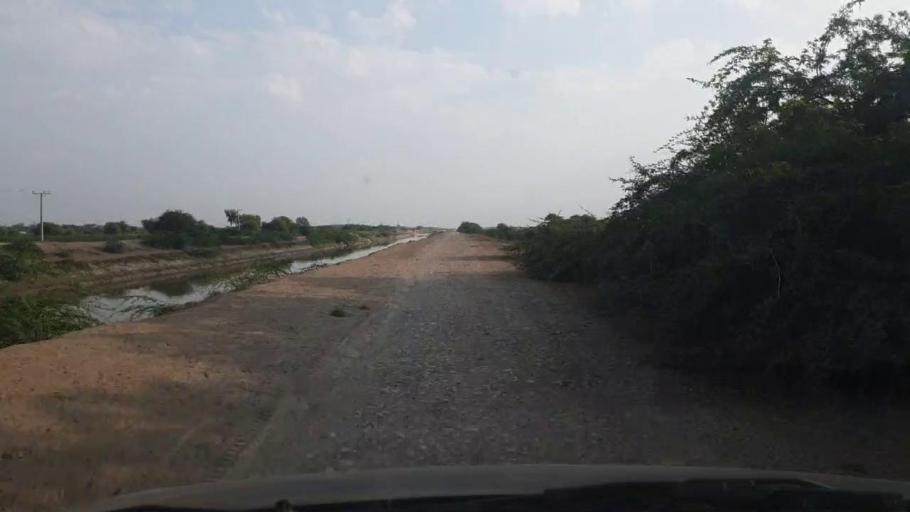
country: PK
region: Sindh
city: Badin
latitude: 24.5177
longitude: 68.6836
